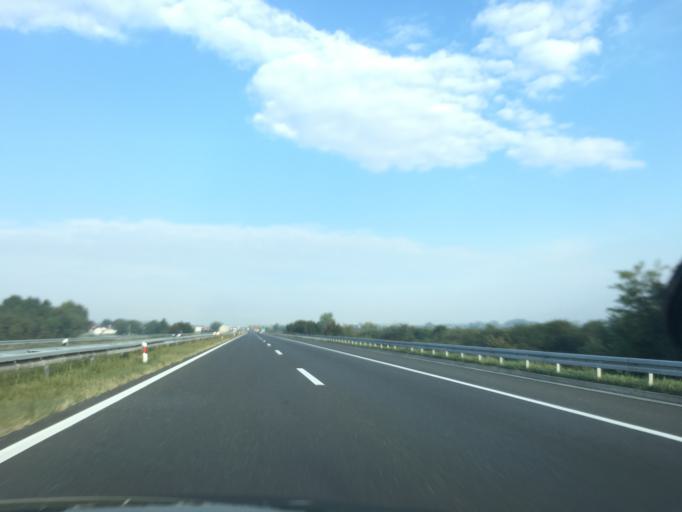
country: HR
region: Zagrebacka
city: Bestovje
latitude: 45.8094
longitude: 15.7687
